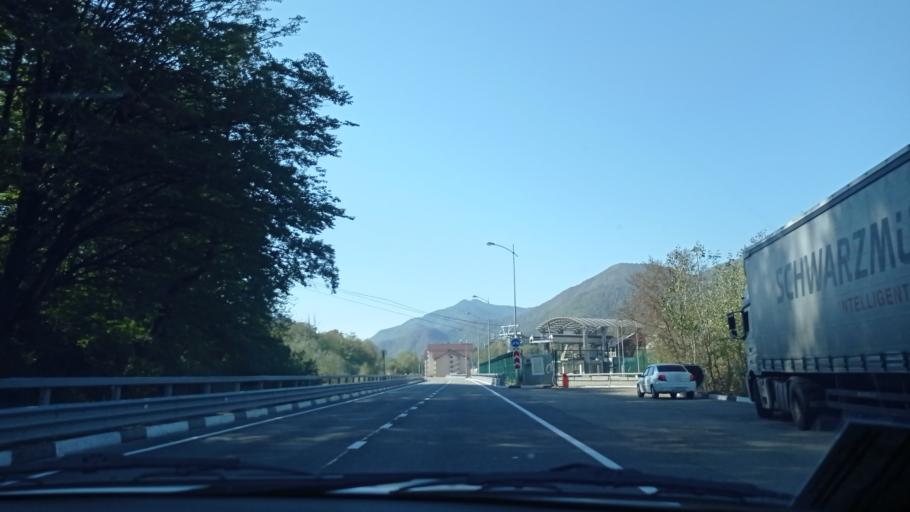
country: RU
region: Krasnodarskiy
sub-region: Sochi City
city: Krasnaya Polyana
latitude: 43.6835
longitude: 40.2365
